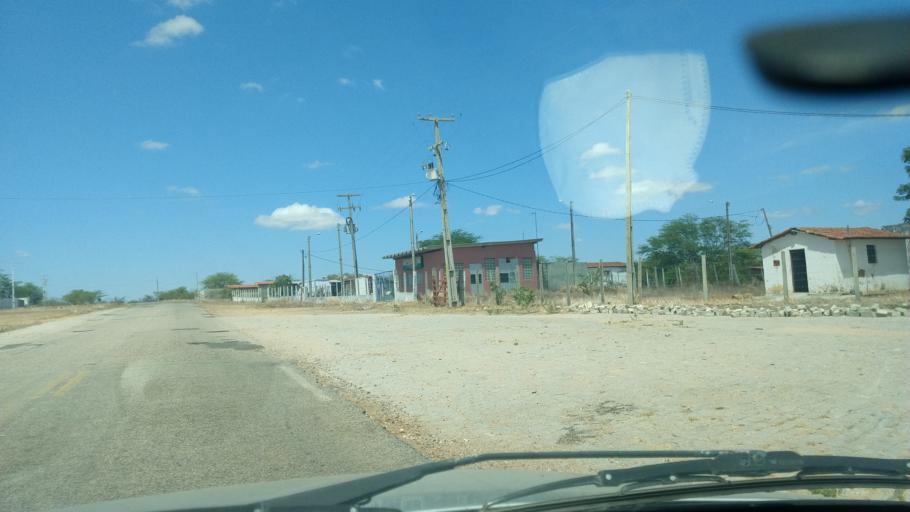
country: BR
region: Rio Grande do Norte
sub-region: Sao Tome
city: Sao Tome
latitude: -5.9694
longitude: -35.9263
